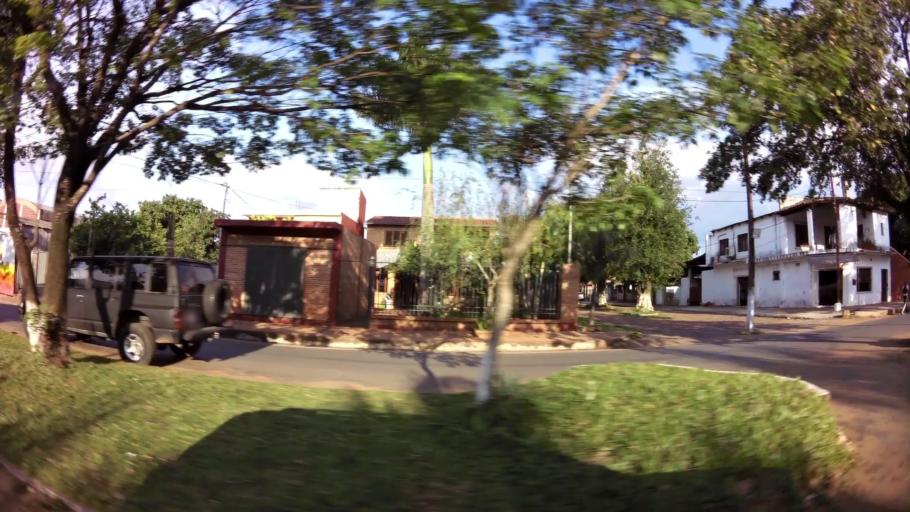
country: PY
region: Central
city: Fernando de la Mora
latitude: -25.3514
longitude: -57.5222
